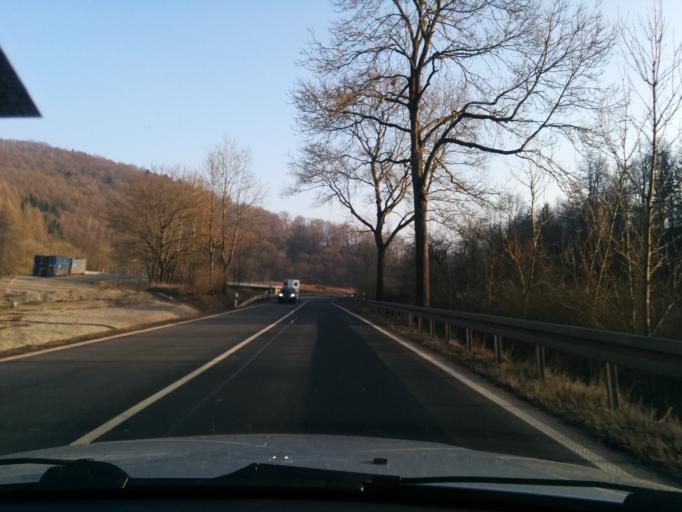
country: DE
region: Hesse
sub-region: Regierungsbezirk Kassel
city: Grossalmerode
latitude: 51.1857
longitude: 9.7972
